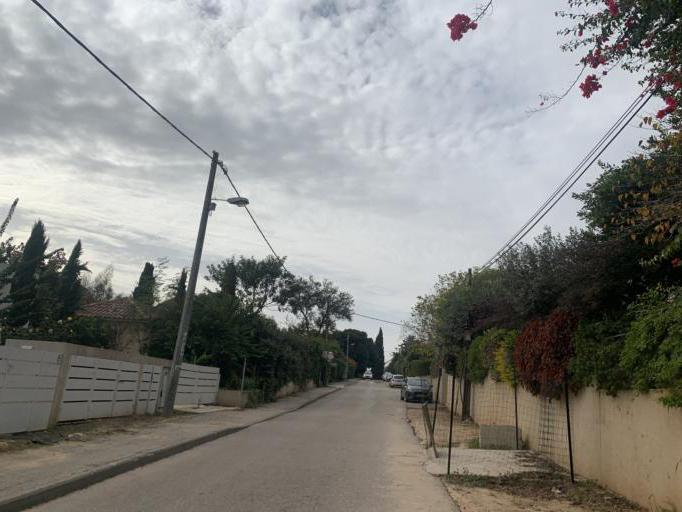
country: IL
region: Central District
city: Hod HaSharon
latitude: 32.1644
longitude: 34.8826
